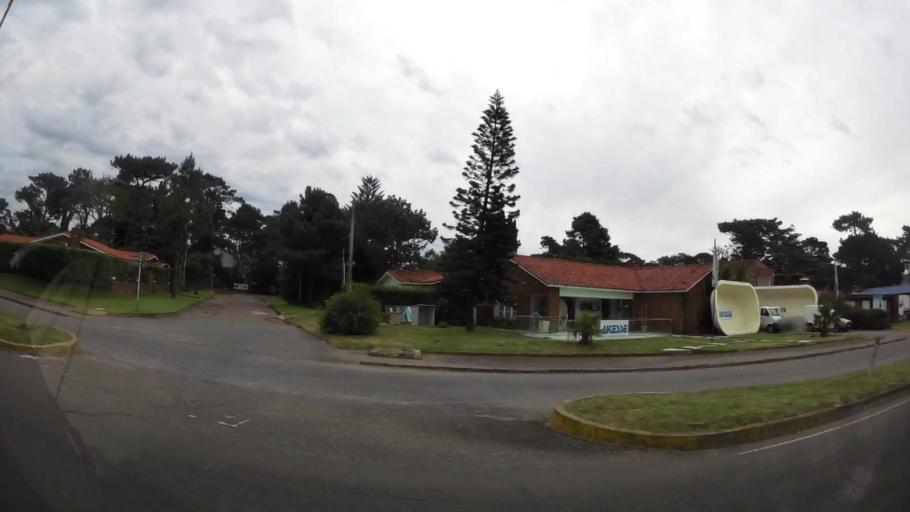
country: UY
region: Maldonado
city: Punta del Este
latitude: -34.9419
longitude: -54.9371
